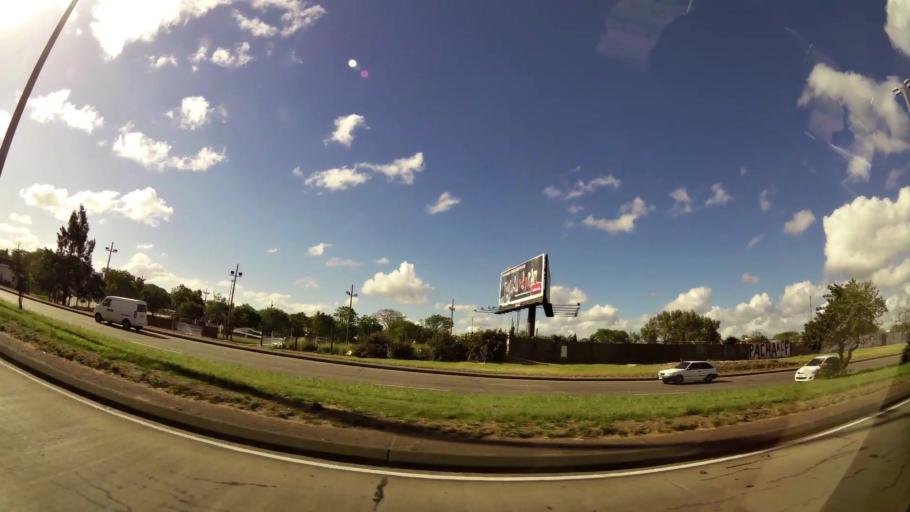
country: UY
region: Montevideo
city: Montevideo
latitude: -34.8689
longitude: -56.2248
